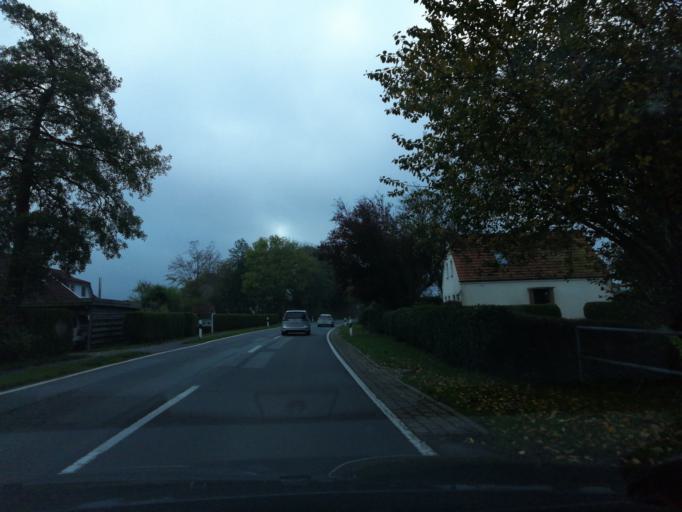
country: DE
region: Lower Saxony
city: Jever
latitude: 53.6795
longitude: 7.8639
